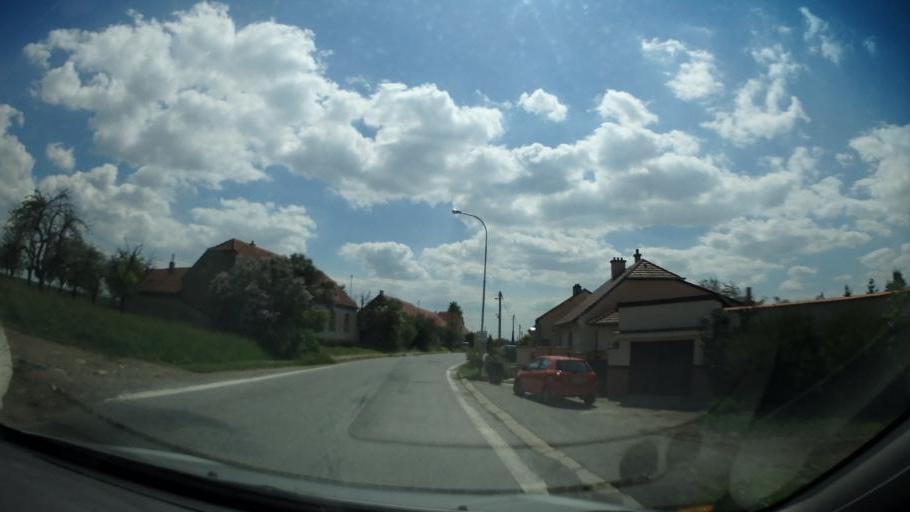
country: CZ
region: Vysocina
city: Hrotovice
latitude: 49.1359
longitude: 16.0805
